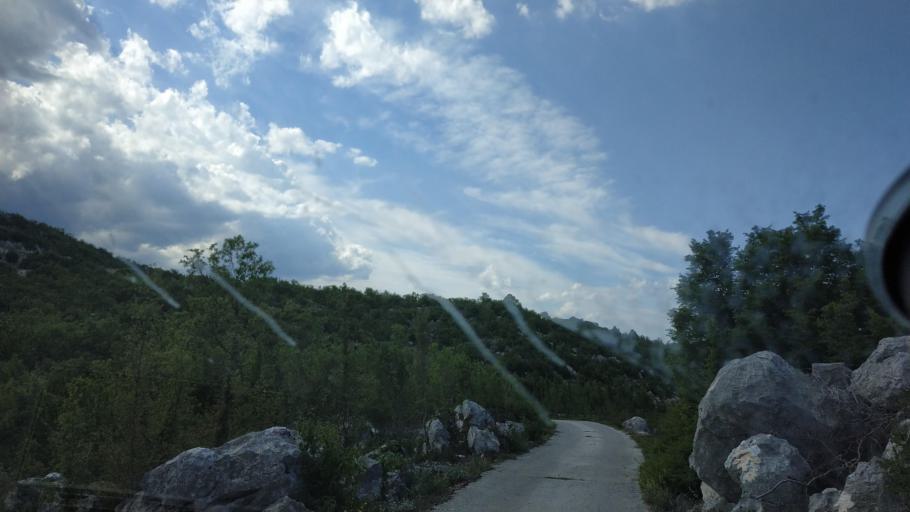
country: HR
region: Splitsko-Dalmatinska
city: Dugopolje
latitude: 43.5705
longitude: 16.6554
